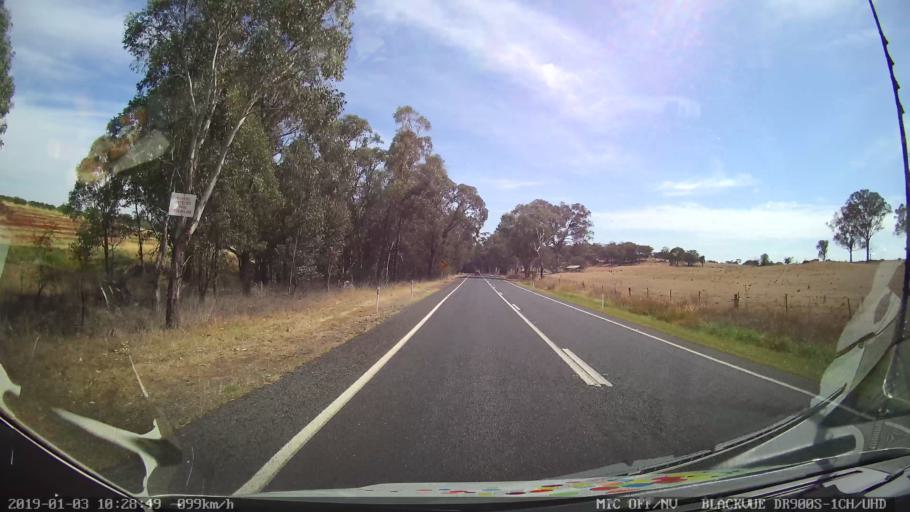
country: AU
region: New South Wales
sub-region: Young
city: Young
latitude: -34.3825
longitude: 148.2598
